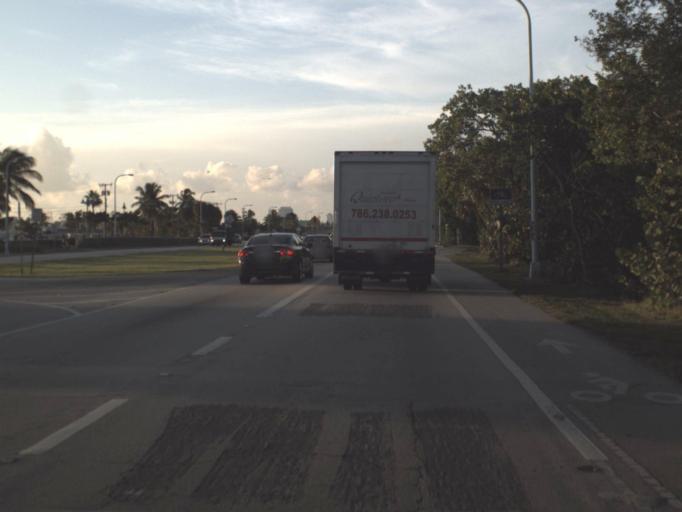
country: US
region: Florida
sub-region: Miami-Dade County
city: Key Biscayne
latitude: 25.7256
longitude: -80.1531
